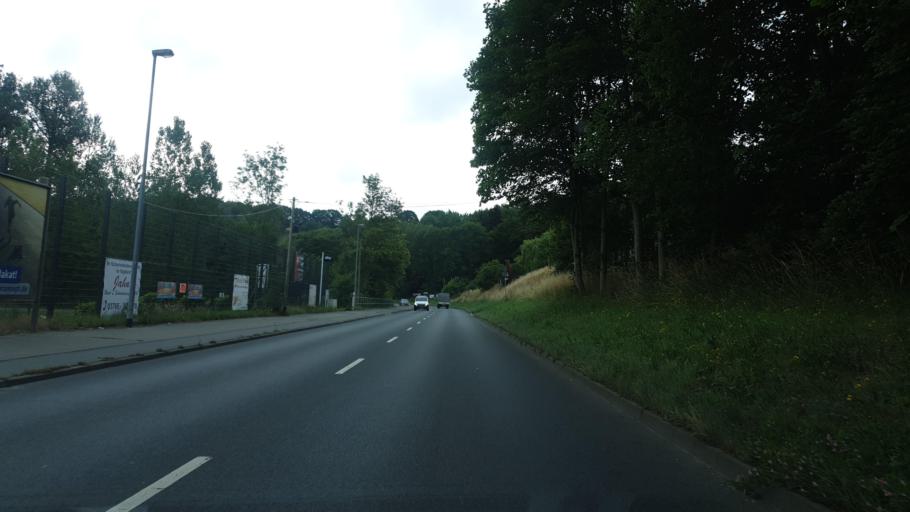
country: DE
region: Saxony
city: Mylau
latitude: 50.6176
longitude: 12.2772
